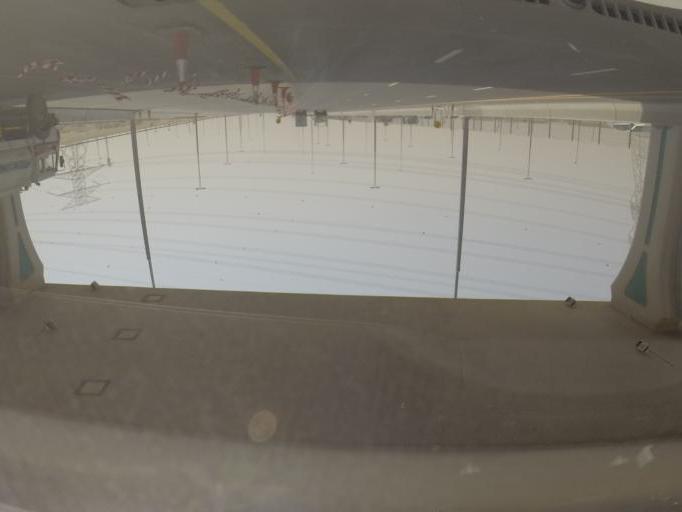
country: AE
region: Dubai
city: Dubai
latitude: 25.0158
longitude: 55.1574
